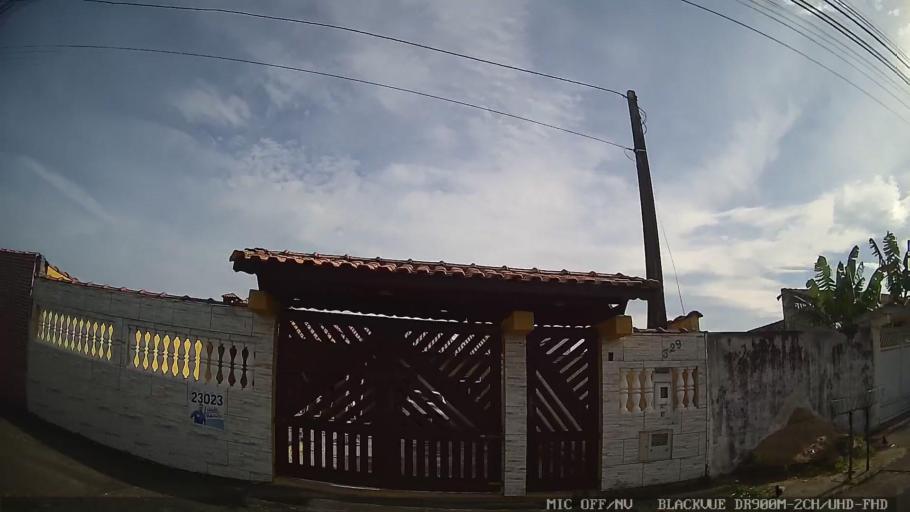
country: BR
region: Sao Paulo
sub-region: Itanhaem
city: Itanhaem
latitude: -24.1647
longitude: -46.7637
